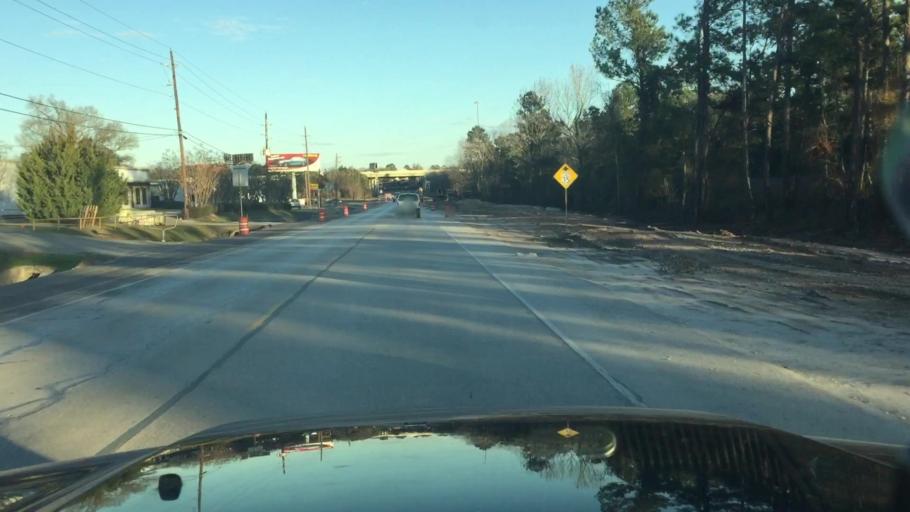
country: US
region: Texas
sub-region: Montgomery County
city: Conroe
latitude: 30.3084
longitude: -95.4757
